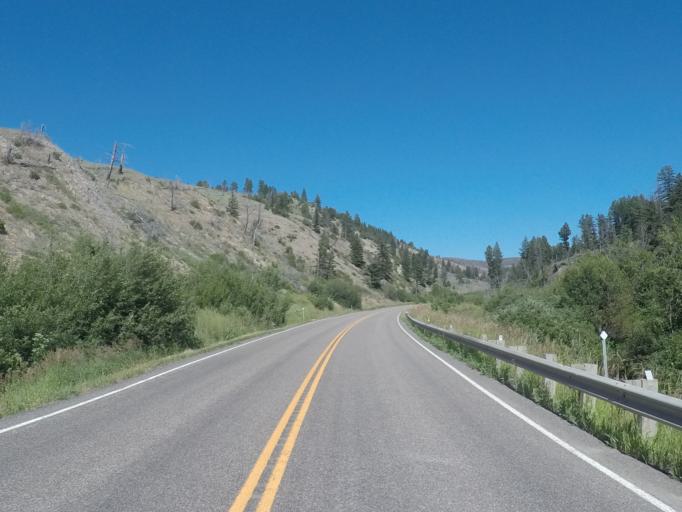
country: US
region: Montana
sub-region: Broadwater County
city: Townsend
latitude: 46.3329
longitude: -111.2488
